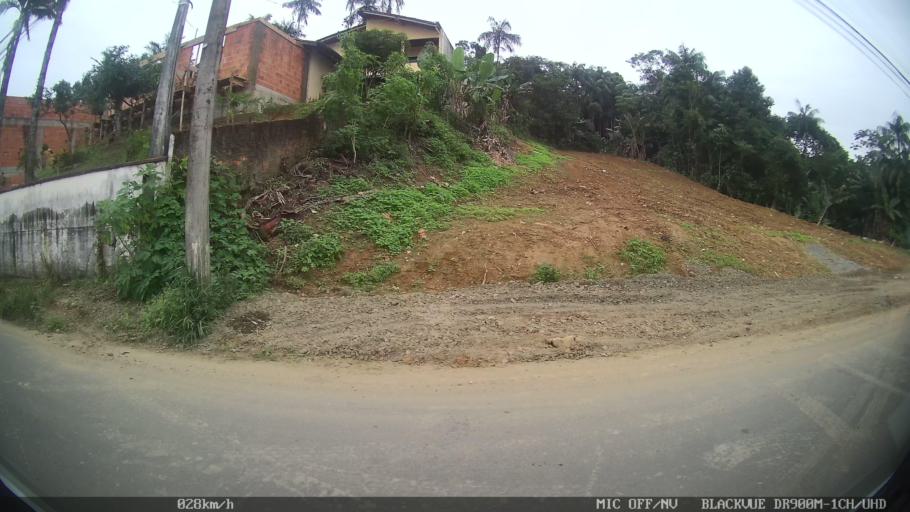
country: BR
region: Santa Catarina
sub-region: Joinville
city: Joinville
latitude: -26.2662
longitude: -48.8258
